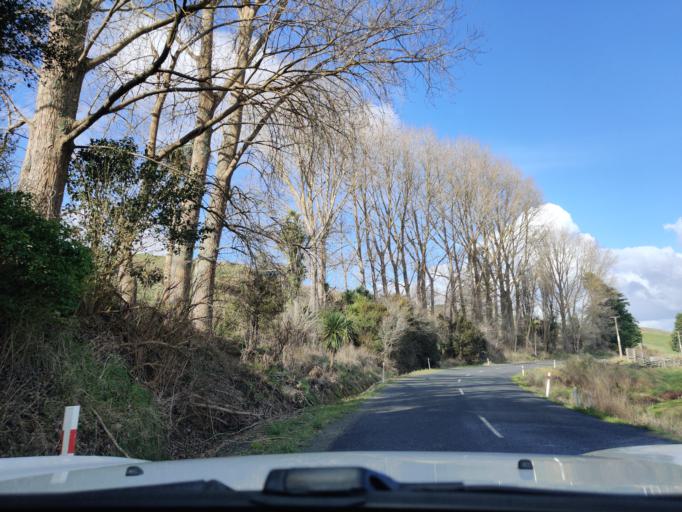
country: NZ
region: Waikato
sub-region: Waikato District
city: Te Kauwhata
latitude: -37.2710
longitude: 175.1992
